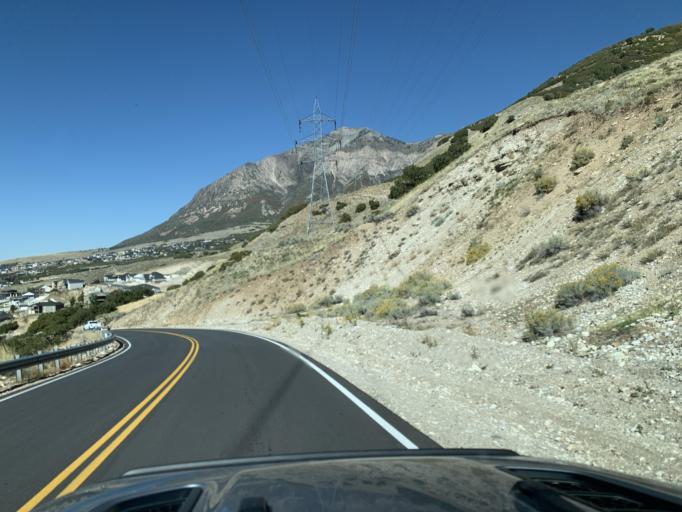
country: US
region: Utah
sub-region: Weber County
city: North Ogden
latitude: 41.3167
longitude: -111.9330
